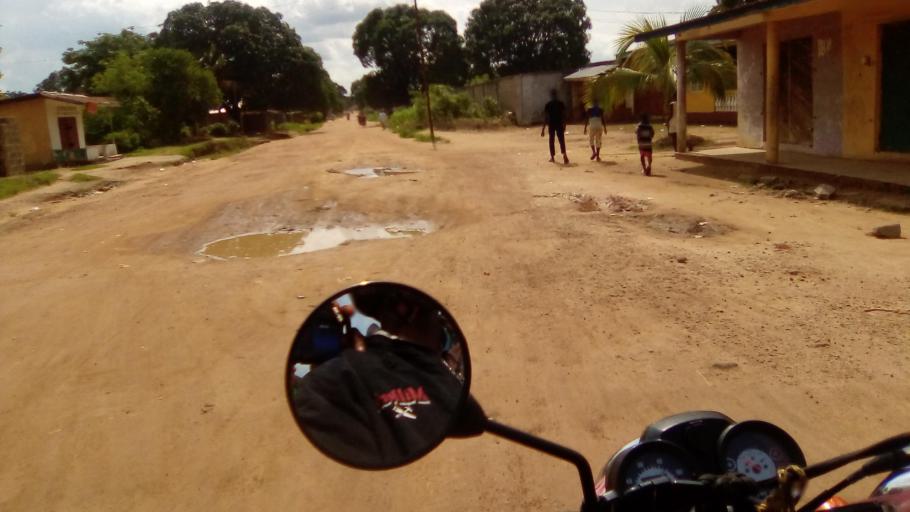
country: SL
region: Southern Province
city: Bo
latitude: 7.9506
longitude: -11.7244
